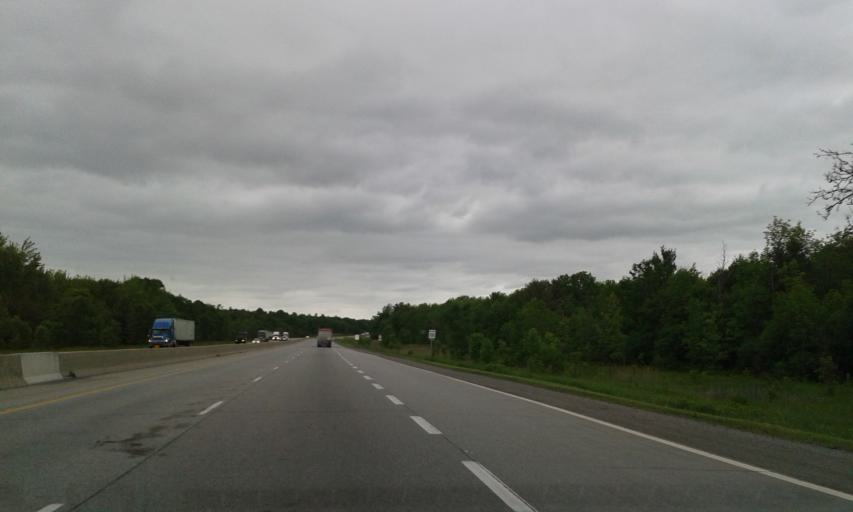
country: CA
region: Ontario
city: Brockville
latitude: 44.5362
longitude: -75.7677
